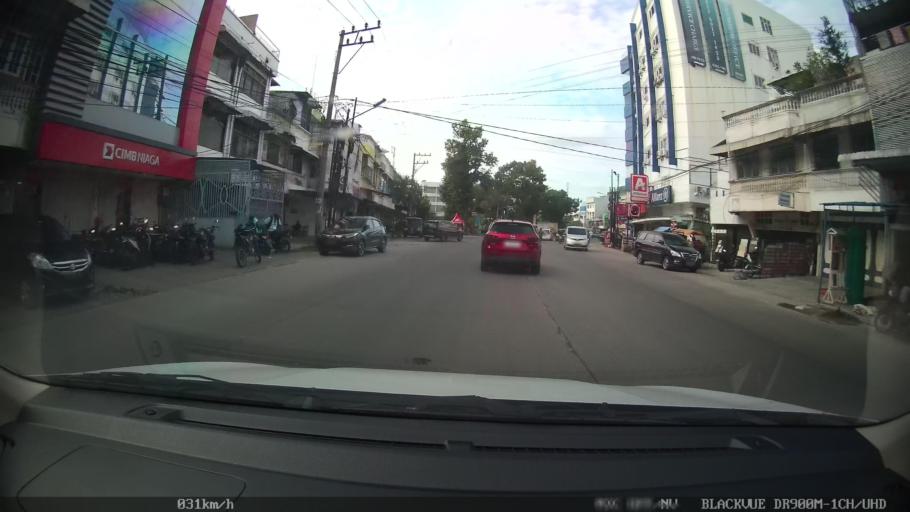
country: ID
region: North Sumatra
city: Medan
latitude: 3.6085
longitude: 98.6799
